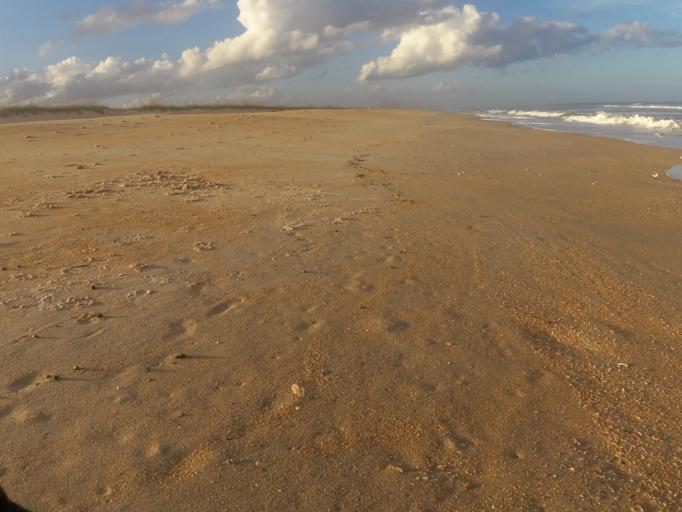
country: US
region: Florida
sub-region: Flagler County
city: Palm Coast
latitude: 29.6343
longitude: -81.1978
